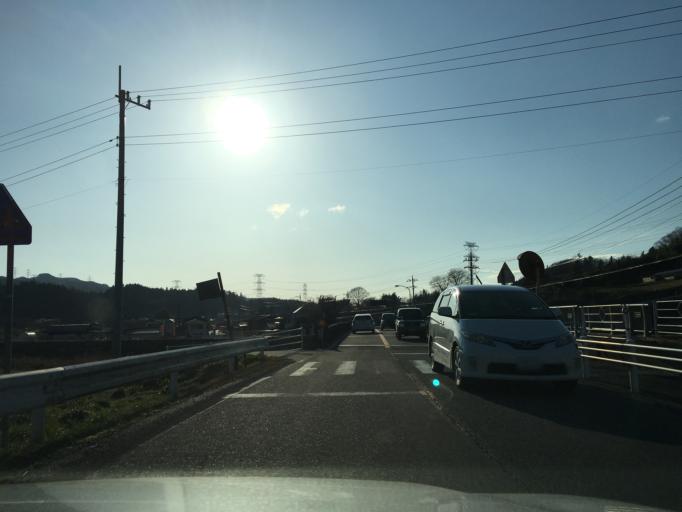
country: JP
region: Ibaraki
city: Daigo
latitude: 36.7776
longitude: 140.3377
